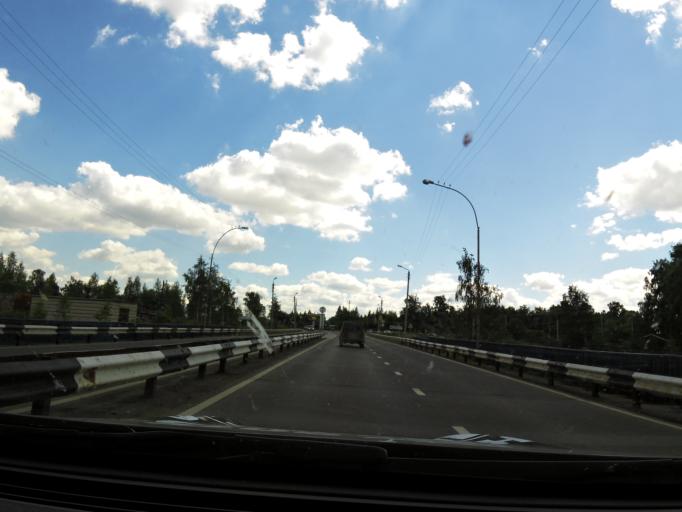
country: RU
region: Vologda
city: Vologda
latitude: 59.2403
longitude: 39.7903
